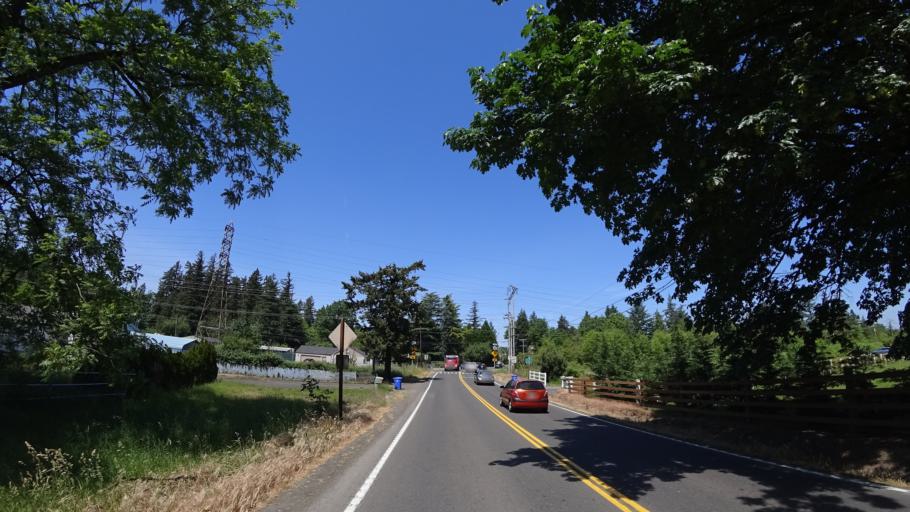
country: US
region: Oregon
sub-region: Multnomah County
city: Gresham
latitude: 45.4850
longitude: -122.4852
